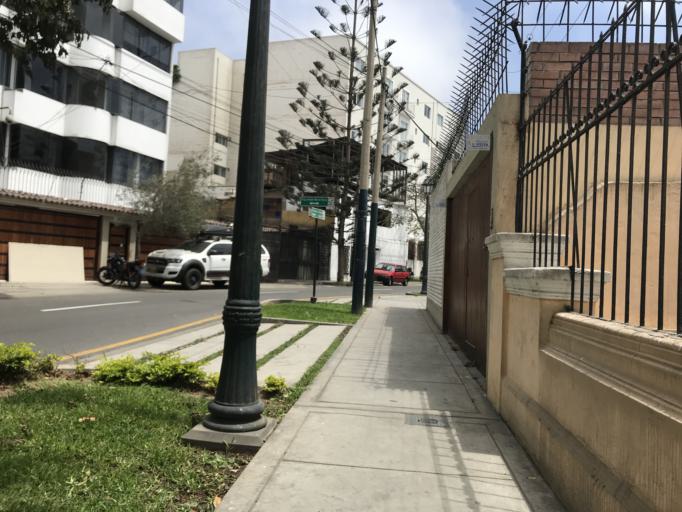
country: PE
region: Lima
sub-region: Lima
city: San Isidro
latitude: -12.1006
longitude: -77.0332
